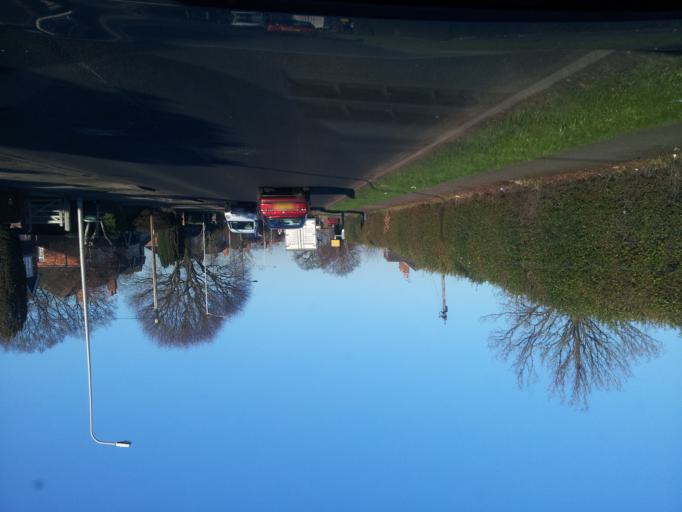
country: GB
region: England
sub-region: West Berkshire
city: Tilehurst
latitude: 51.4519
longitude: -1.0464
